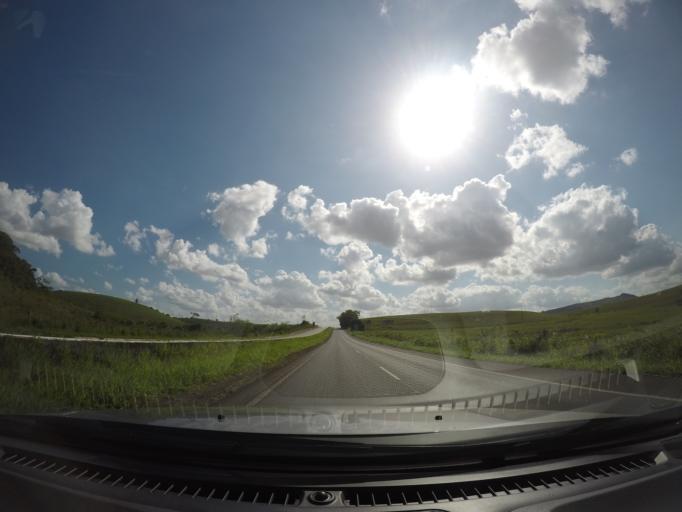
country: BR
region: Pernambuco
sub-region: Joaquim Nabuco
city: Joaquim Nabuco
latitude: -8.5816
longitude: -35.4964
